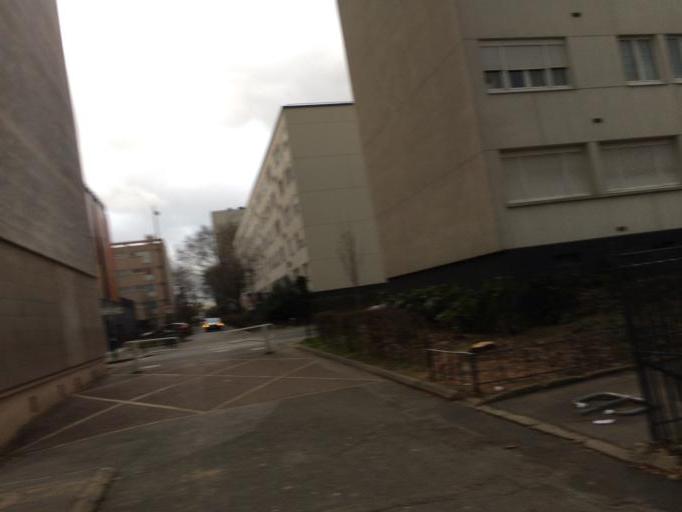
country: FR
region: Ile-de-France
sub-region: Departement de l'Essonne
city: Massy
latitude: 48.7350
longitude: 2.2937
